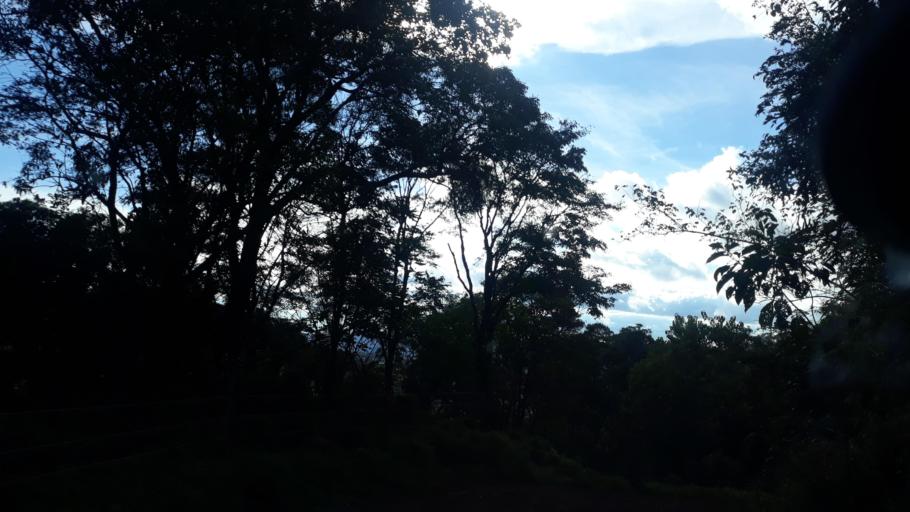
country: AR
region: Misiones
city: Bernardo de Irigoyen
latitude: -26.2721
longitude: -53.6668
